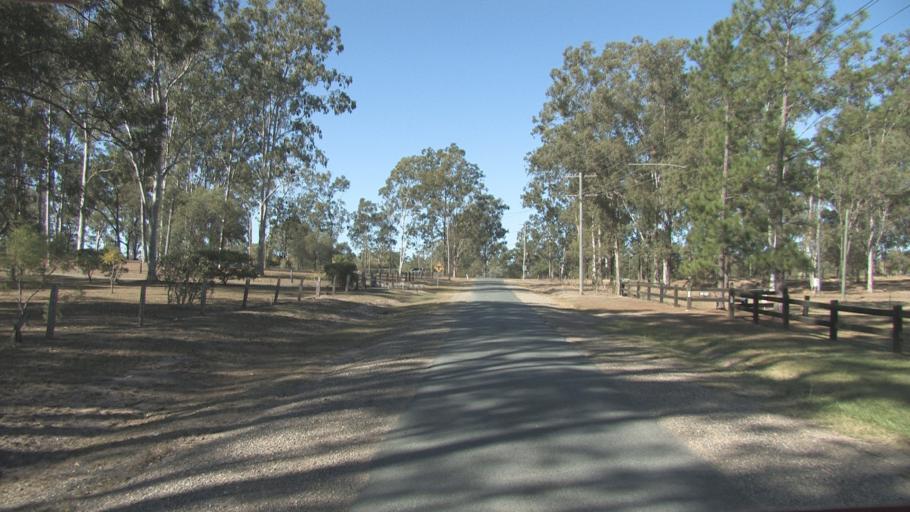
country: AU
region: Queensland
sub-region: Logan
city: Cedar Vale
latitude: -27.8575
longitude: 153.0301
